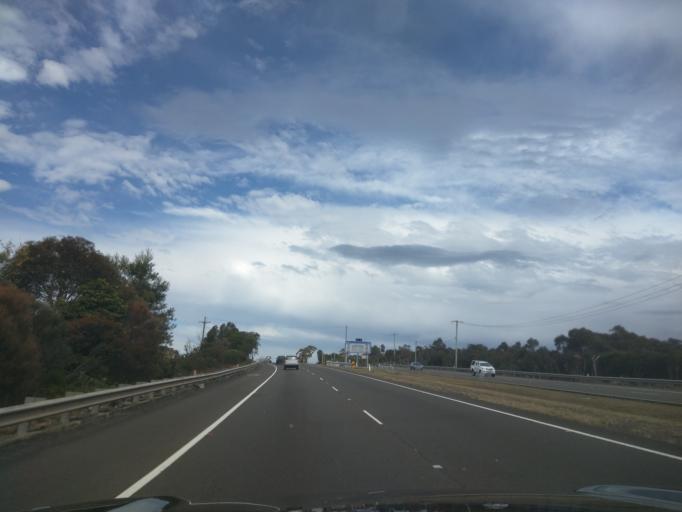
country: AU
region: New South Wales
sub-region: Sutherland Shire
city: Heathcote
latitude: -34.1039
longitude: 150.9941
